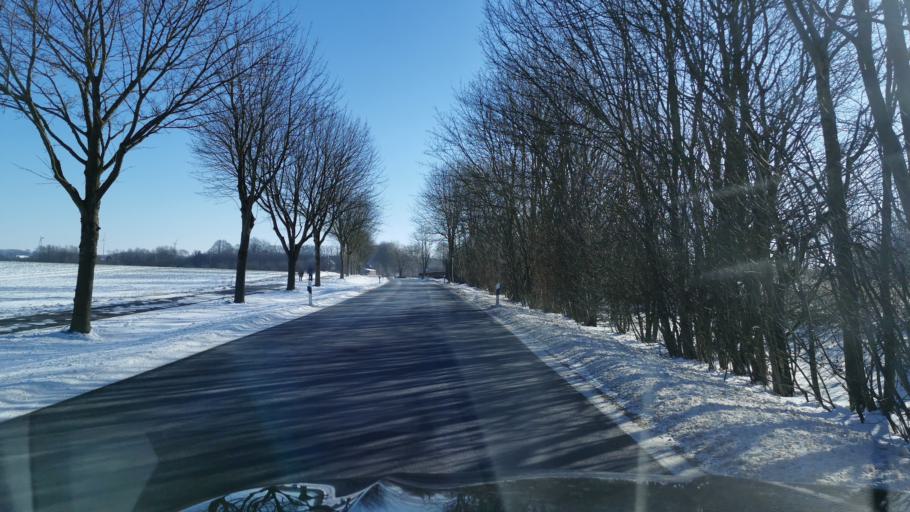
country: DE
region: Schleswig-Holstein
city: Grundhof
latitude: 54.7775
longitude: 9.6482
